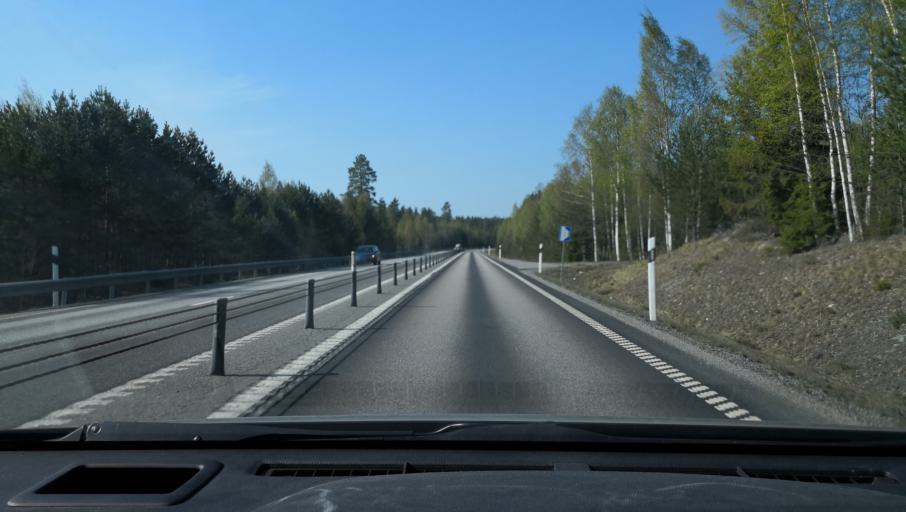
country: SE
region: Uppsala
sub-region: Heby Kommun
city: Tarnsjo
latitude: 60.1778
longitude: 16.9487
